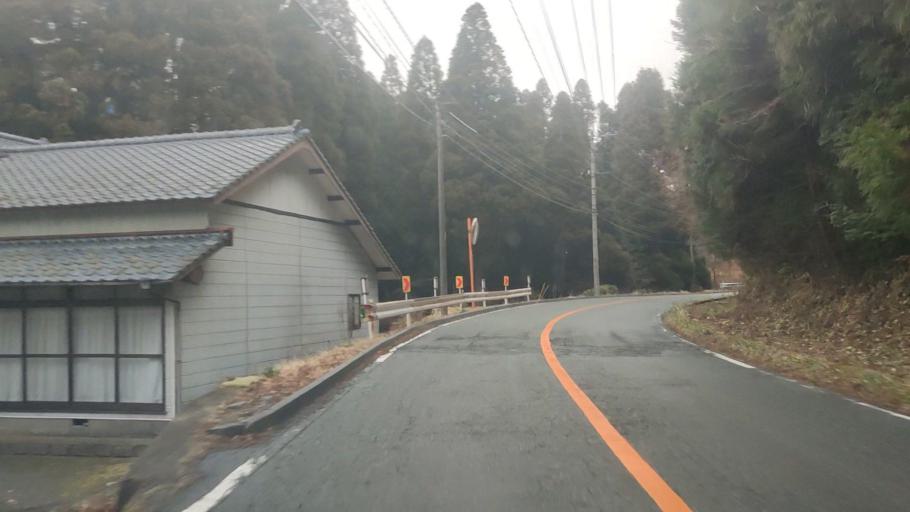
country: JP
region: Kumamoto
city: Aso
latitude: 32.8591
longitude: 131.1620
